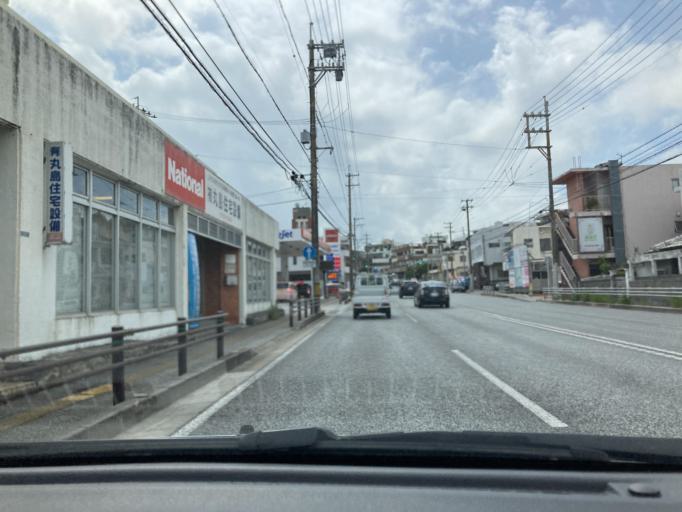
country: JP
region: Okinawa
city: Okinawa
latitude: 26.3237
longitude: 127.8224
